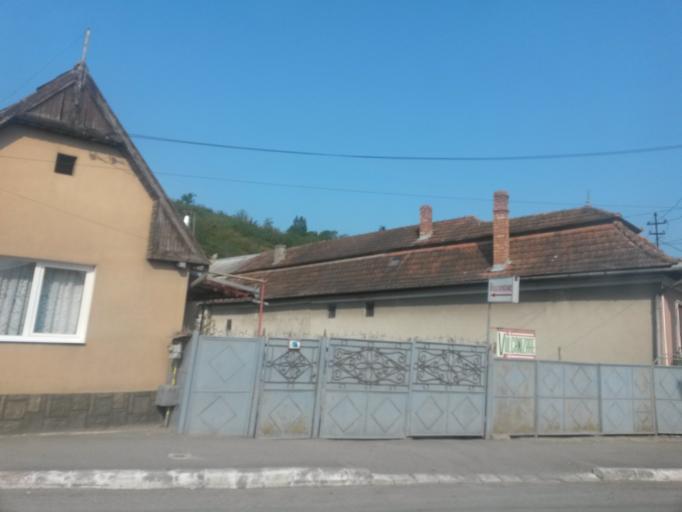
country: RO
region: Cluj
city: Turda
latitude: 46.5822
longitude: 23.7652
